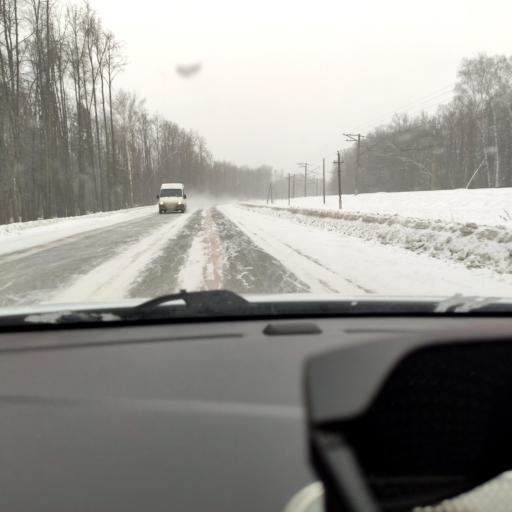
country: RU
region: Tatarstan
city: Vysokaya Gora
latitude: 55.9185
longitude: 49.2817
